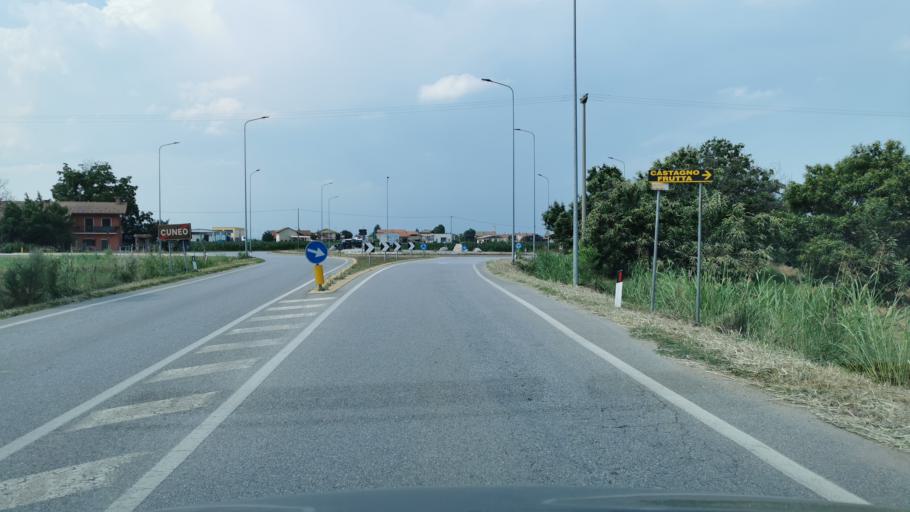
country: IT
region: Piedmont
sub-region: Provincia di Cuneo
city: Tarantasca
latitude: 44.4847
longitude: 7.5441
